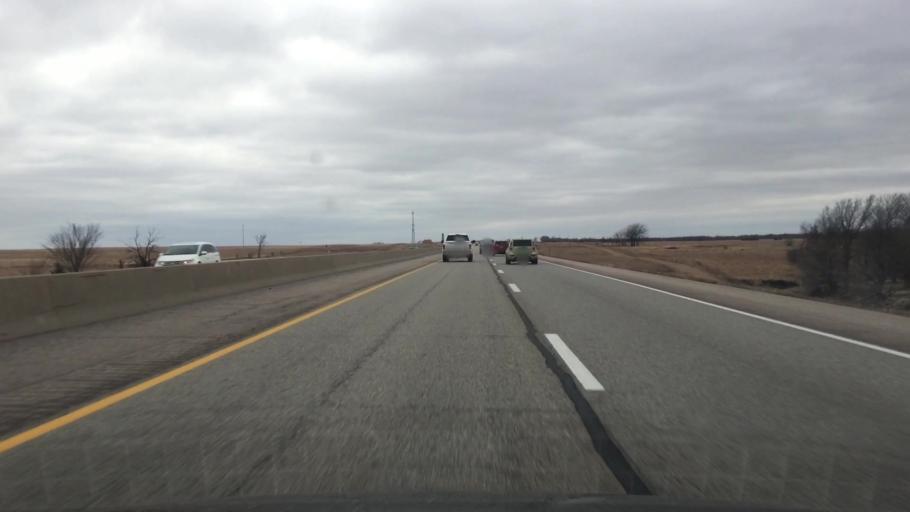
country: US
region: Kansas
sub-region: Butler County
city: El Dorado
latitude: 37.9720
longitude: -96.7206
